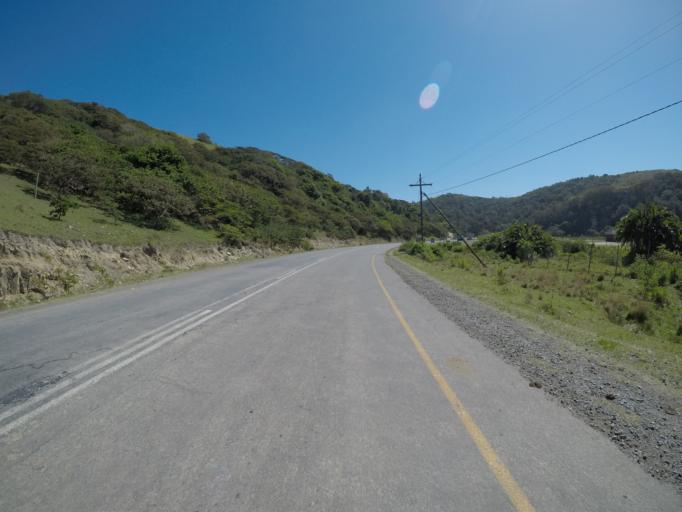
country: ZA
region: Eastern Cape
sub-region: OR Tambo District Municipality
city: Libode
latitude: -31.9803
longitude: 29.1477
